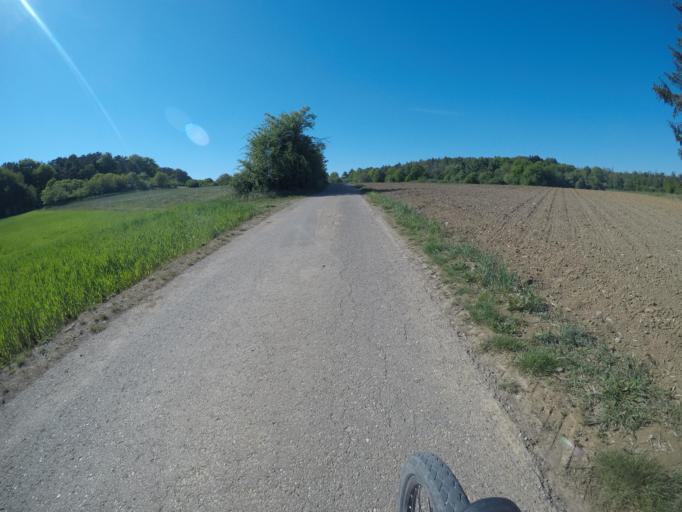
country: DE
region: Baden-Wuerttemberg
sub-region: Karlsruhe Region
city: Friolzheim
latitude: 48.8225
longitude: 8.8514
